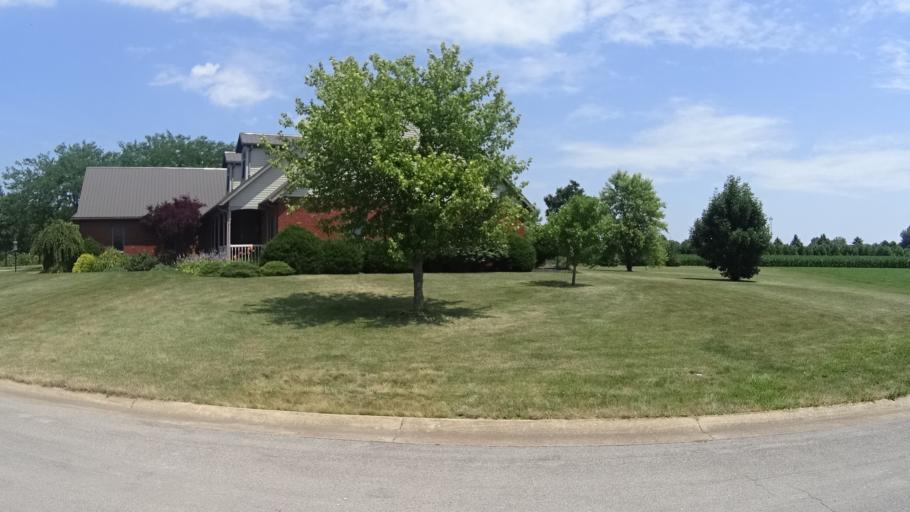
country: US
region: Ohio
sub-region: Erie County
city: Huron
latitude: 41.4107
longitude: -82.6209
